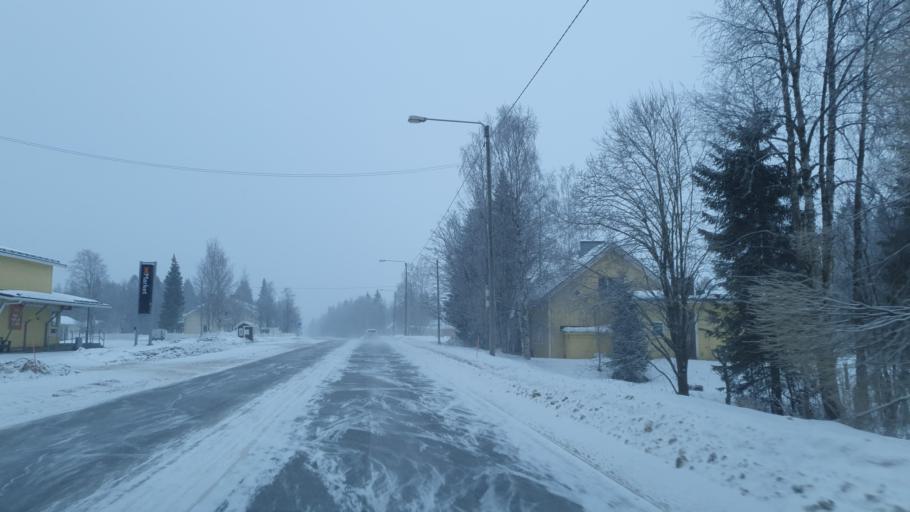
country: FI
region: Lapland
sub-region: Kemi-Tornio
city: Tornio
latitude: 66.0419
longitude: 24.0167
